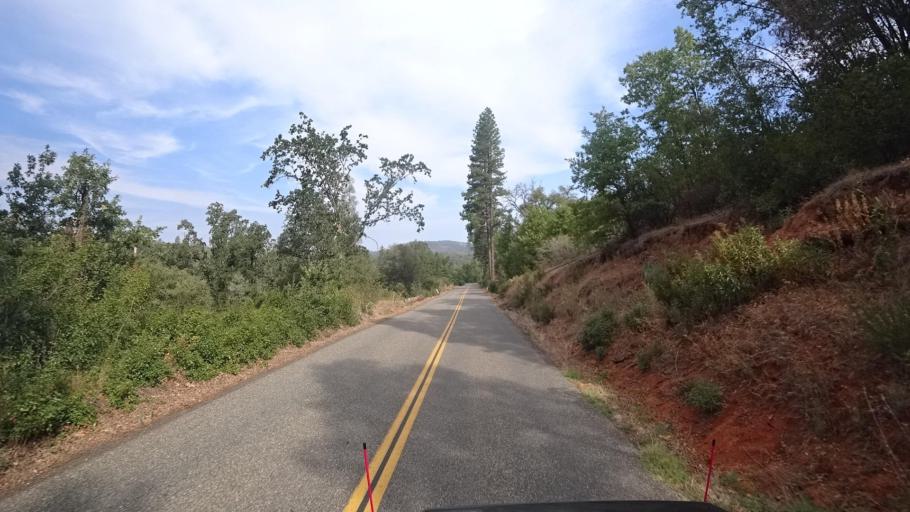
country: US
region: California
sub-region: Mariposa County
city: Midpines
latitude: 37.5156
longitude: -119.9164
